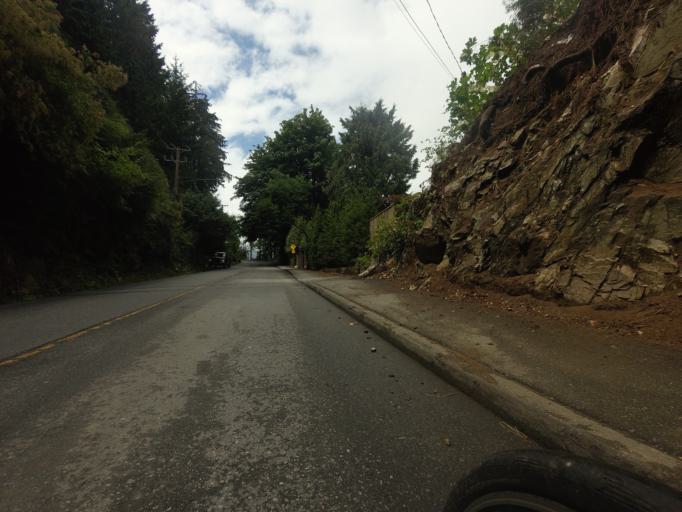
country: CA
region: British Columbia
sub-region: Greater Vancouver Regional District
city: Bowen Island
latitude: 49.3521
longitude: -123.2625
